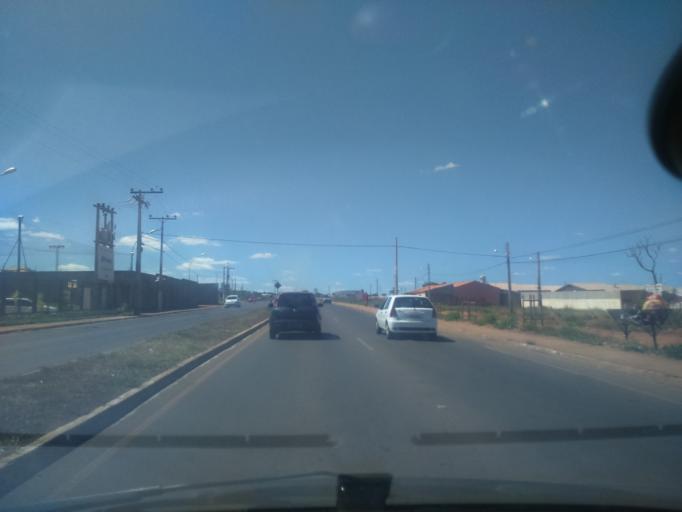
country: BR
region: Goias
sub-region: Luziania
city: Luziania
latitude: -16.1008
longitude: -47.9571
